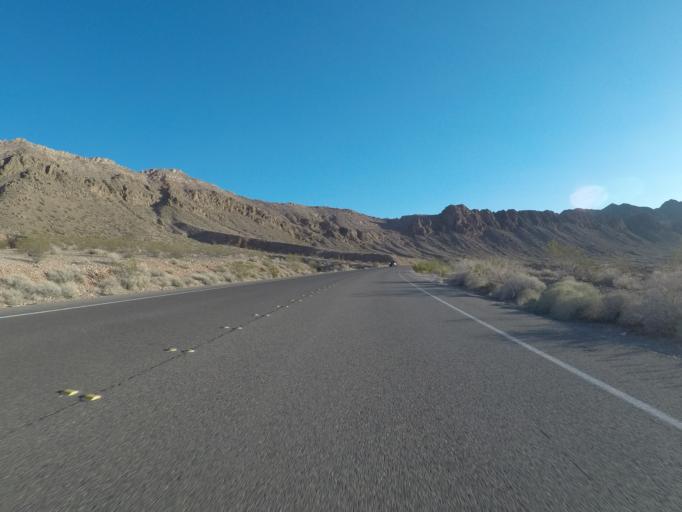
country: US
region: Nevada
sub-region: Clark County
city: Moapa Valley
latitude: 36.2572
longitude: -114.4822
